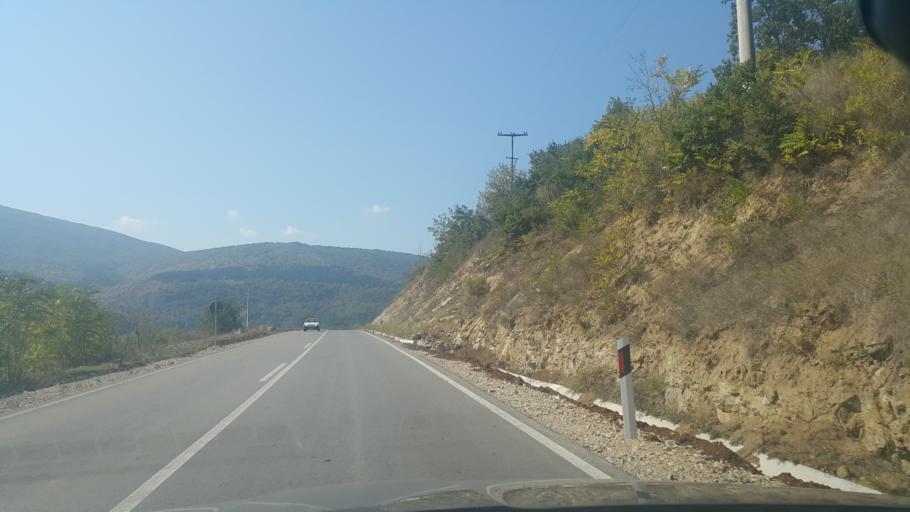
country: RS
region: Central Serbia
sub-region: Pirotski Okrug
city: Pirot
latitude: 43.2148
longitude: 22.5125
